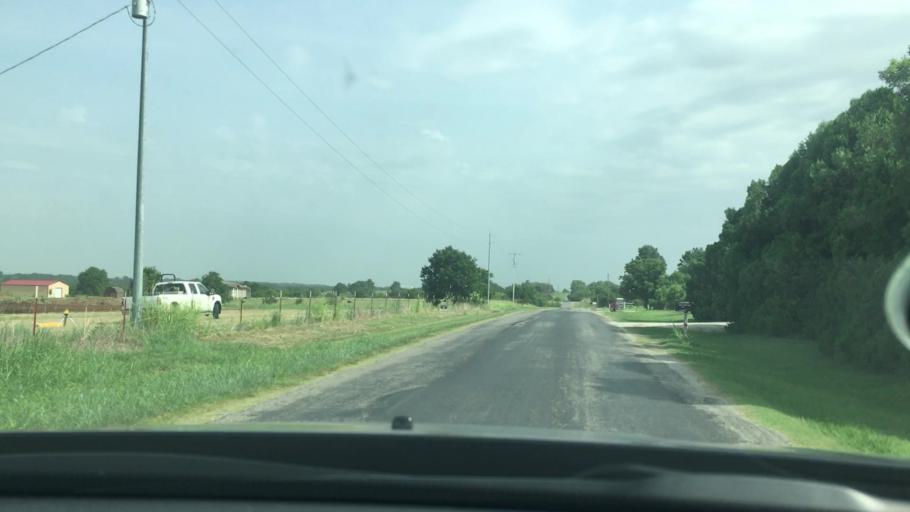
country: US
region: Oklahoma
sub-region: Garvin County
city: Pauls Valley
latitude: 34.8130
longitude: -97.1956
